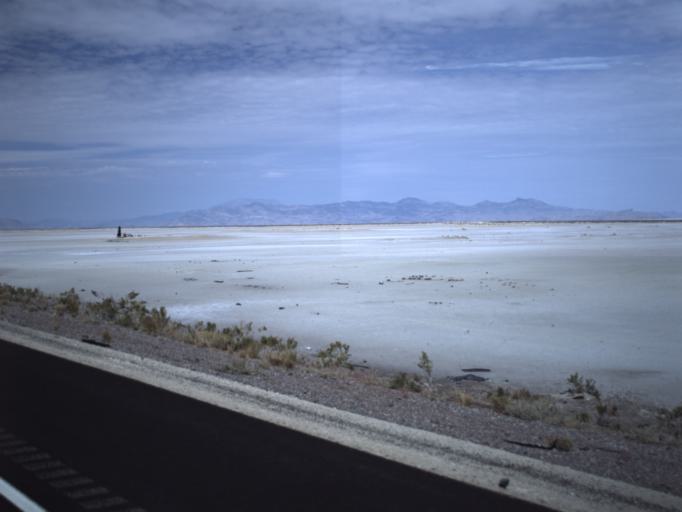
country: US
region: Utah
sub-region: Tooele County
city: Wendover
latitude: 40.7313
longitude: -113.4794
